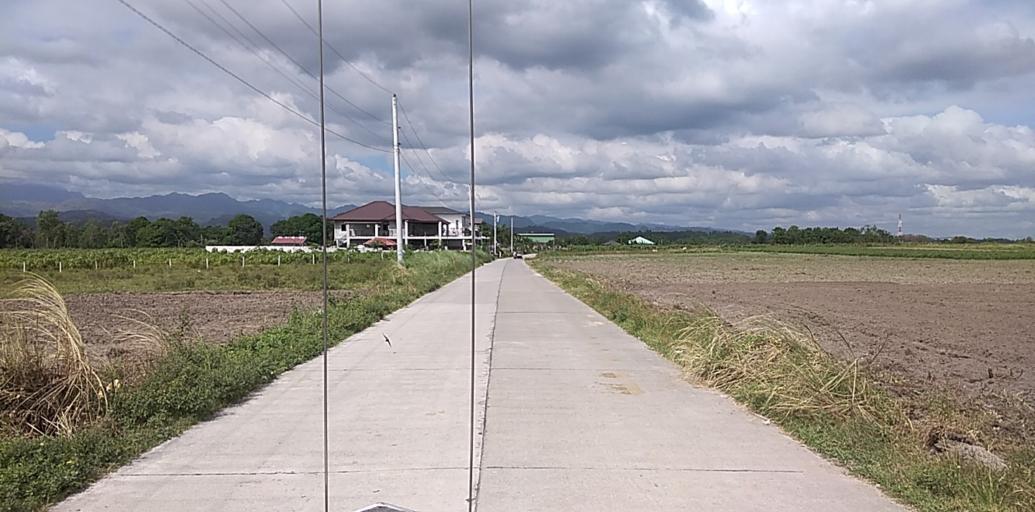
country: PH
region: Central Luzon
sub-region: Province of Pampanga
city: Porac
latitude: 15.0595
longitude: 120.5390
